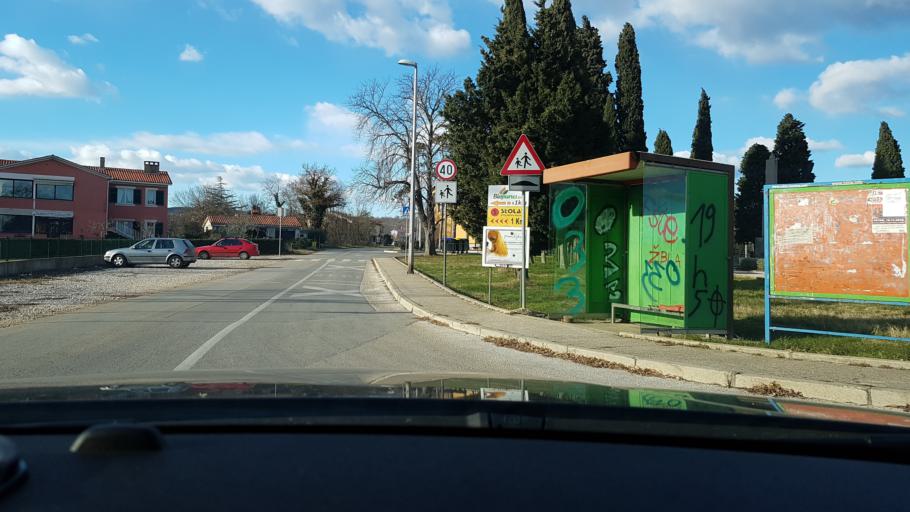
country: HR
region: Istarska
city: Vinez
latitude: 45.1010
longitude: 14.1054
